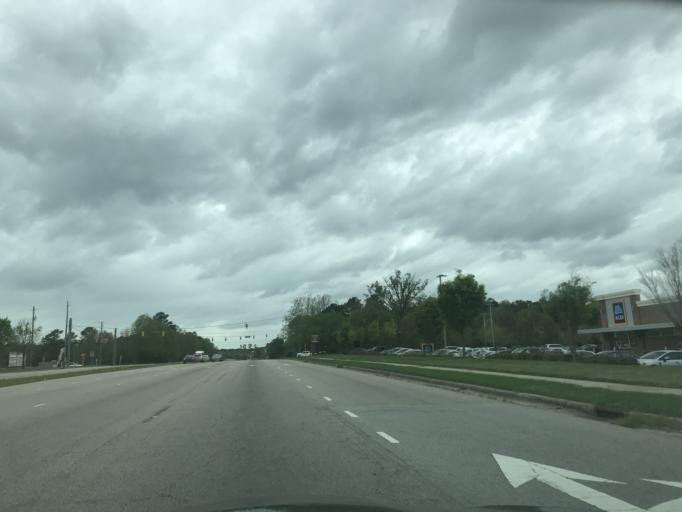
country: US
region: North Carolina
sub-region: Wake County
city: Knightdale
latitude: 35.7932
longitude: -78.5472
